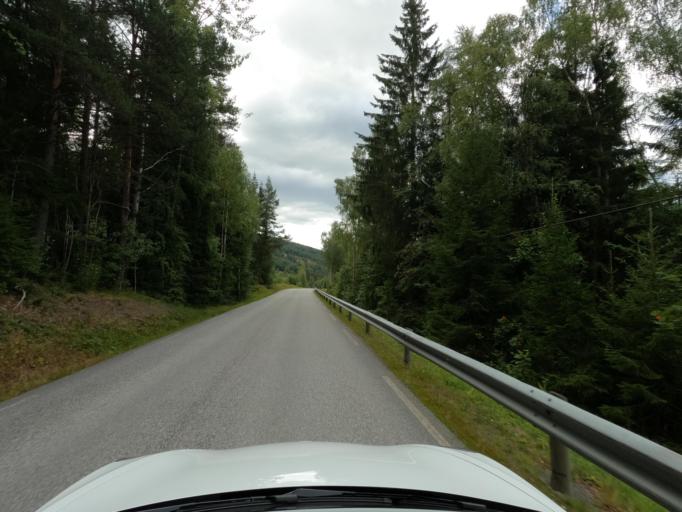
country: NO
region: Buskerud
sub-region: Nore og Uvdal
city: Rodberg
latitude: 60.0221
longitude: 8.8346
